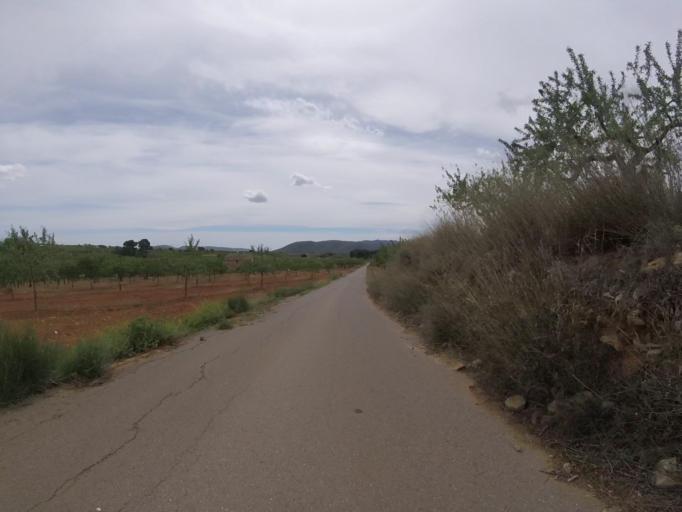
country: ES
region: Valencia
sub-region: Provincia de Castello
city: Benlloch
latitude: 40.1814
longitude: -0.0074
